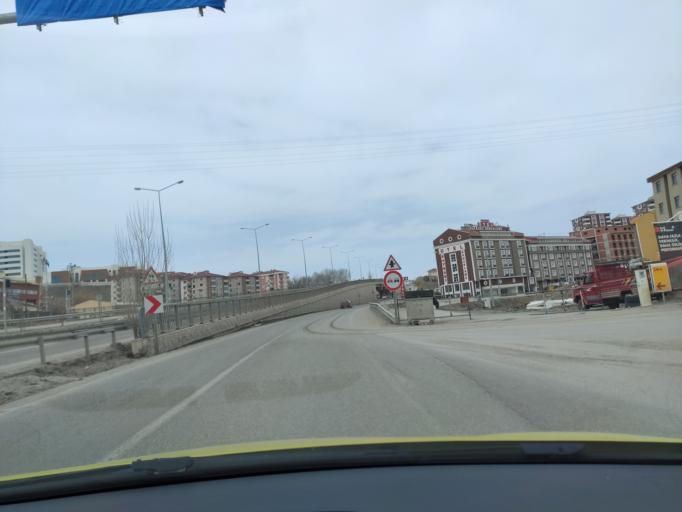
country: TR
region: Bayburt
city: Bayburt
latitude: 40.2579
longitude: 40.2149
